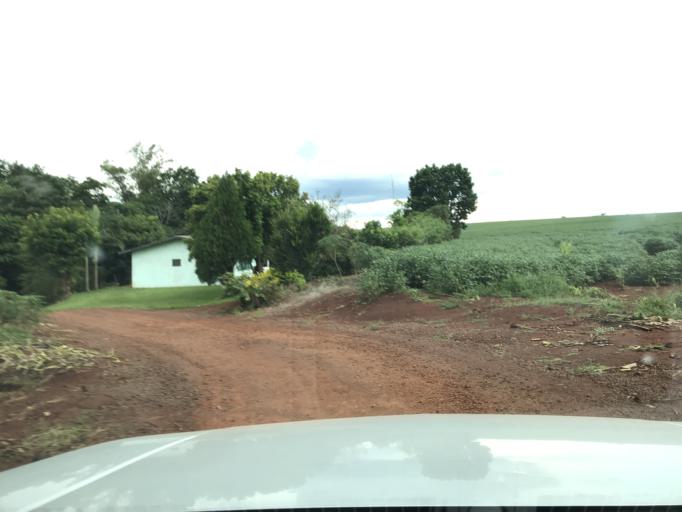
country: BR
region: Parana
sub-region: Palotina
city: Palotina
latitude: -24.2749
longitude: -53.7892
